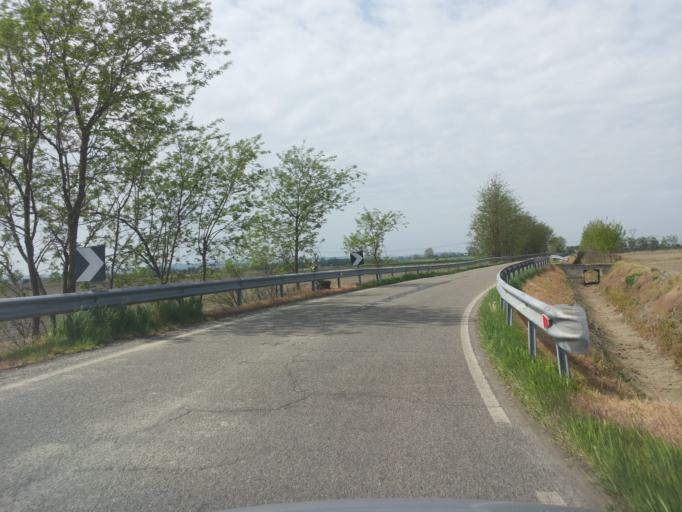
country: IT
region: Piedmont
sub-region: Provincia di Vercelli
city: Motta De Conti
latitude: 45.1863
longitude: 8.5093
